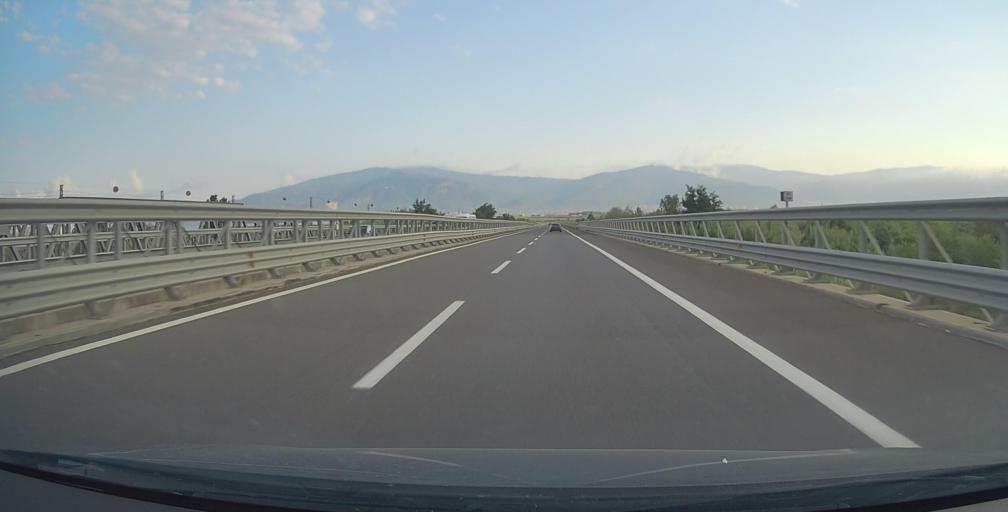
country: IT
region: Calabria
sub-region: Provincia di Catanzaro
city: Santa Eufemia Lamezia
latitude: 38.8942
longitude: 16.2792
